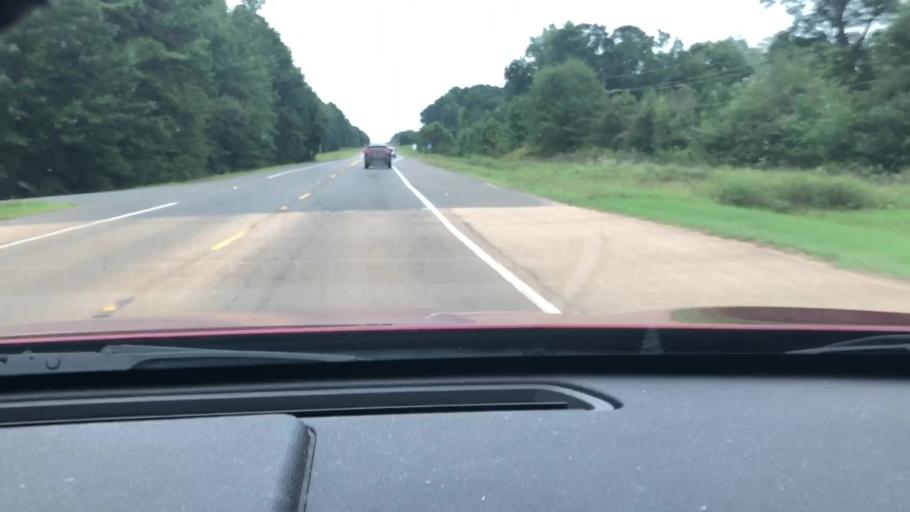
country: US
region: Arkansas
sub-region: Lafayette County
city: Stamps
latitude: 33.3646
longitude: -93.4736
